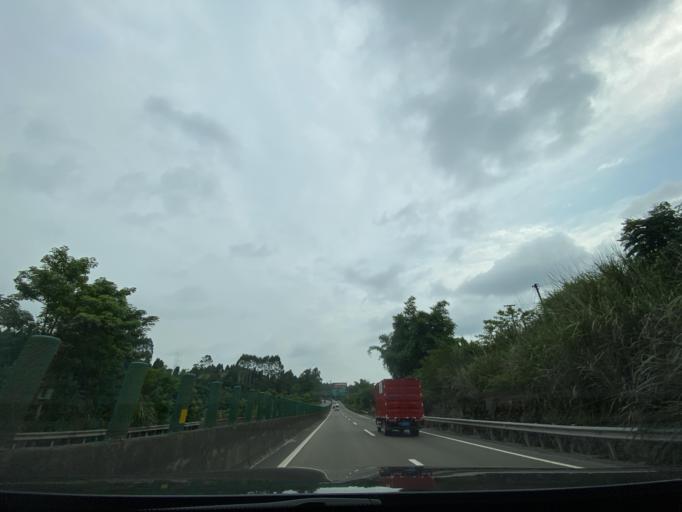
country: CN
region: Sichuan
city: Neijiang
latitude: 29.6382
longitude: 104.9843
